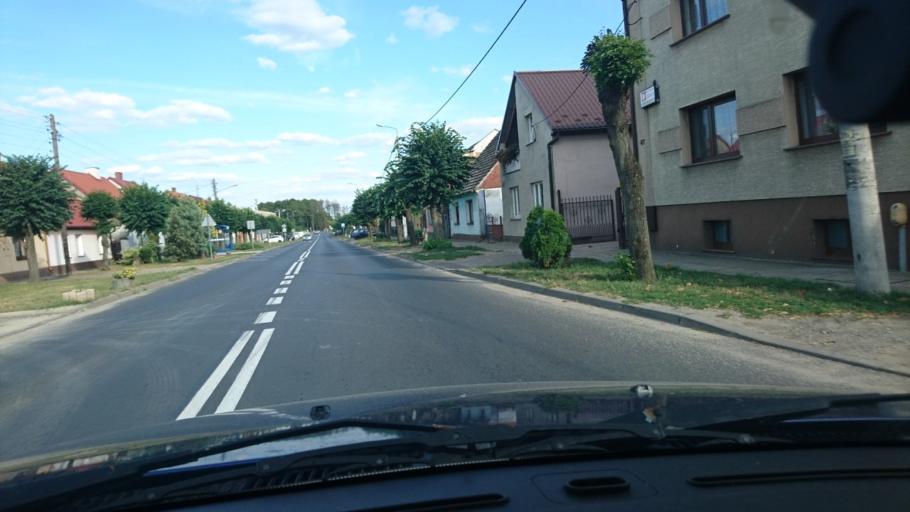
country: PL
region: Greater Poland Voivodeship
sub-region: Powiat krotoszynski
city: Sulmierzyce
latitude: 51.6099
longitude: 17.5186
